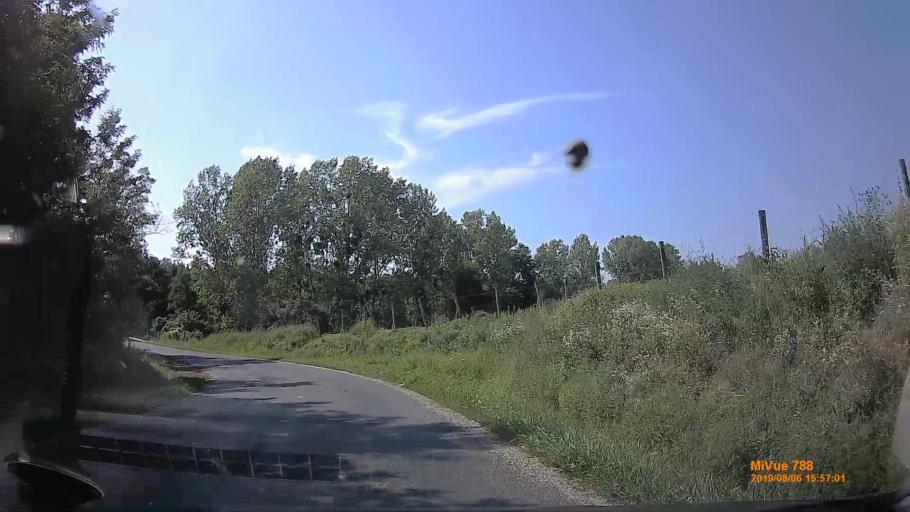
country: HU
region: Somogy
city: Csurgo
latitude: 46.2937
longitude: 17.0066
